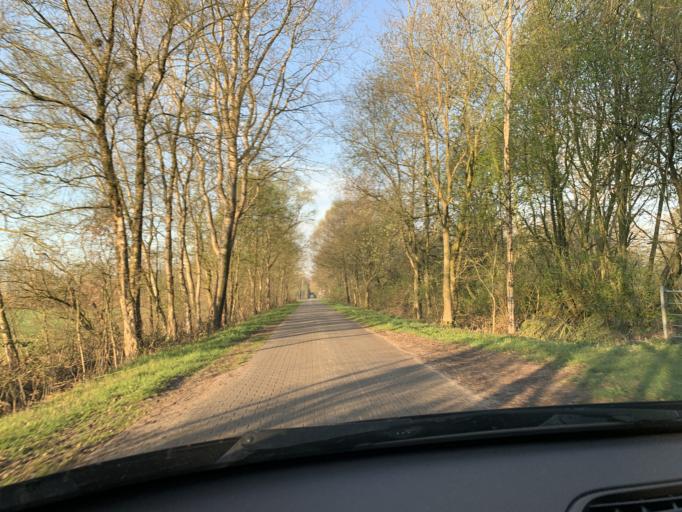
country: DE
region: Lower Saxony
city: Apen
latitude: 53.2799
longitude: 7.8170
